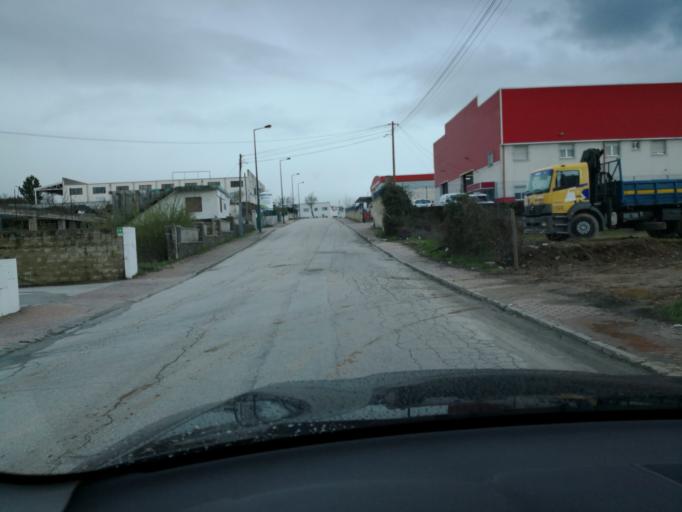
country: PT
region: Vila Real
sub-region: Vila Real
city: Vila Real
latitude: 41.2784
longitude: -7.7085
